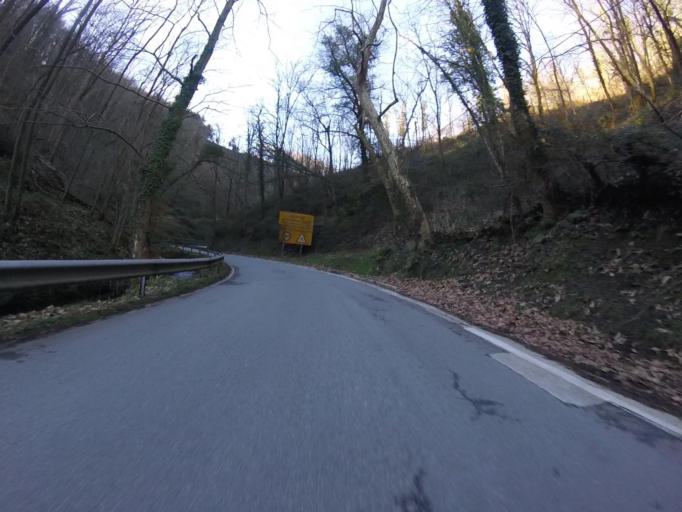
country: ES
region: Navarre
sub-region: Provincia de Navarra
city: Lesaka
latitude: 43.2486
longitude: -1.7203
